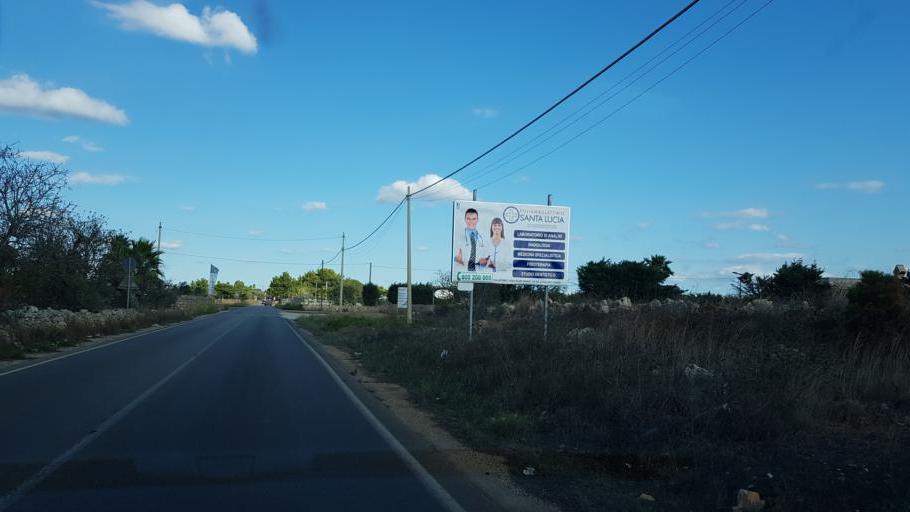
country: IT
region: Apulia
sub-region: Provincia di Lecce
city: Nardo
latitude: 40.1282
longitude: 18.0258
